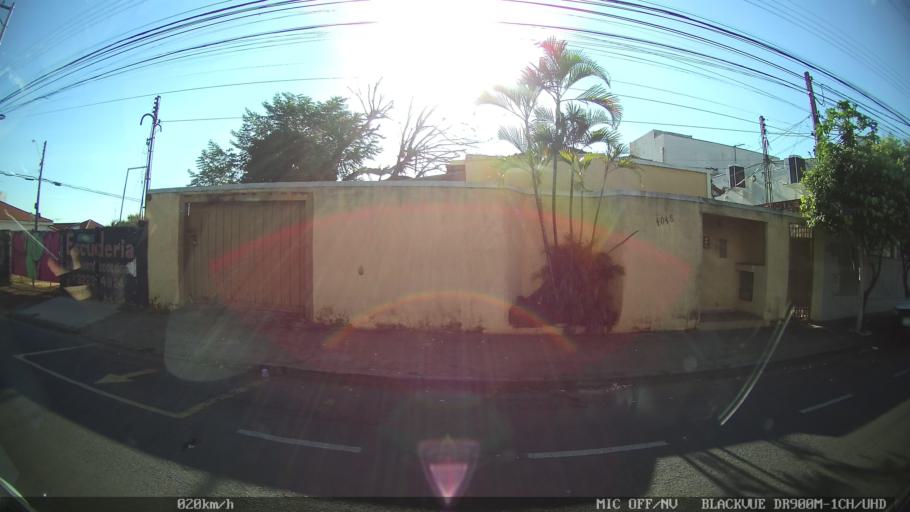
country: BR
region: Sao Paulo
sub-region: Sao Jose Do Rio Preto
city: Sao Jose do Rio Preto
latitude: -20.7978
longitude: -49.3679
